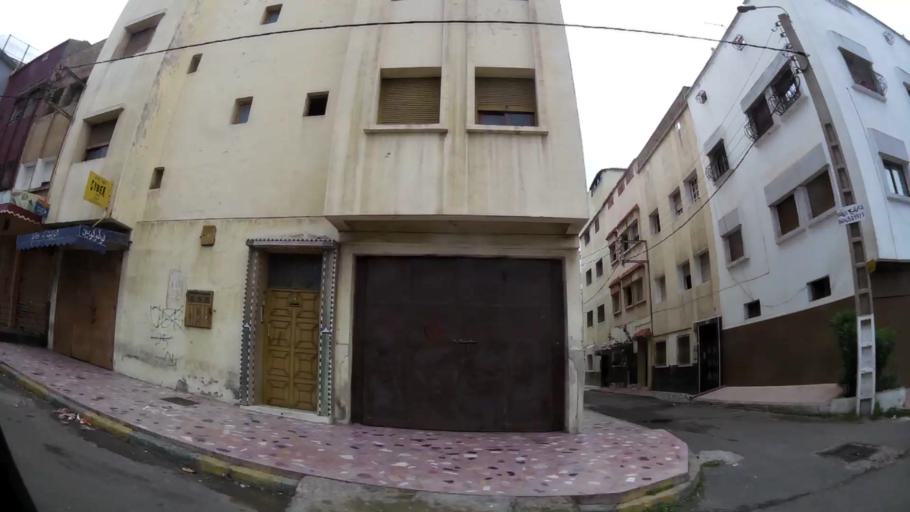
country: MA
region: Grand Casablanca
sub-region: Mediouna
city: Tit Mellil
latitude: 33.6138
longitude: -7.4913
